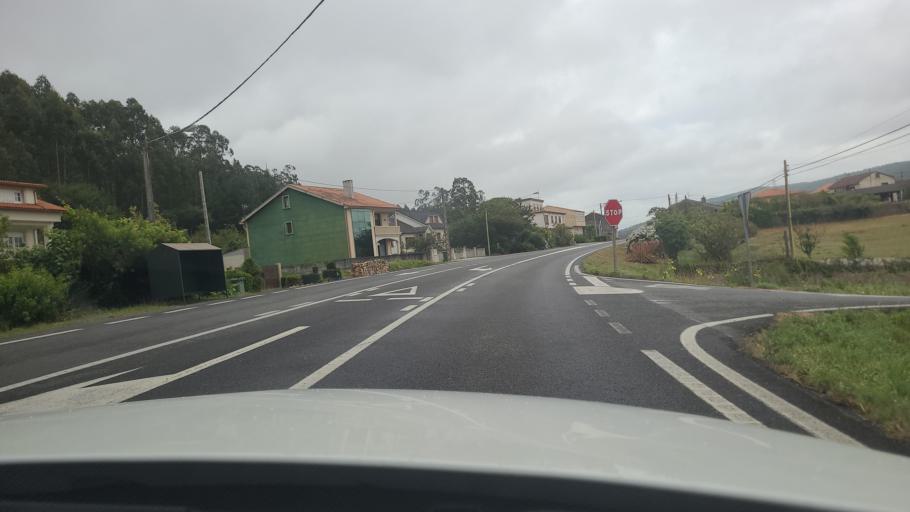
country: ES
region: Galicia
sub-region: Provincia da Coruna
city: Cee
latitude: 42.9967
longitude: -9.1793
